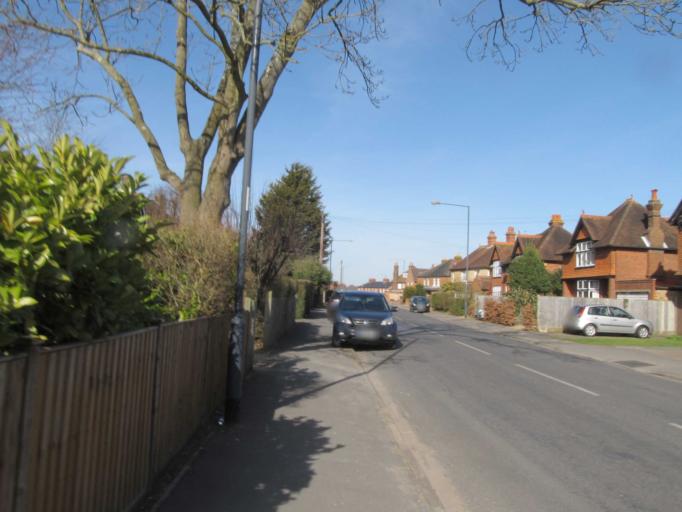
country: GB
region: England
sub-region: Royal Borough of Windsor and Maidenhead
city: Maidenhead
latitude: 51.5331
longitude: -0.7381
